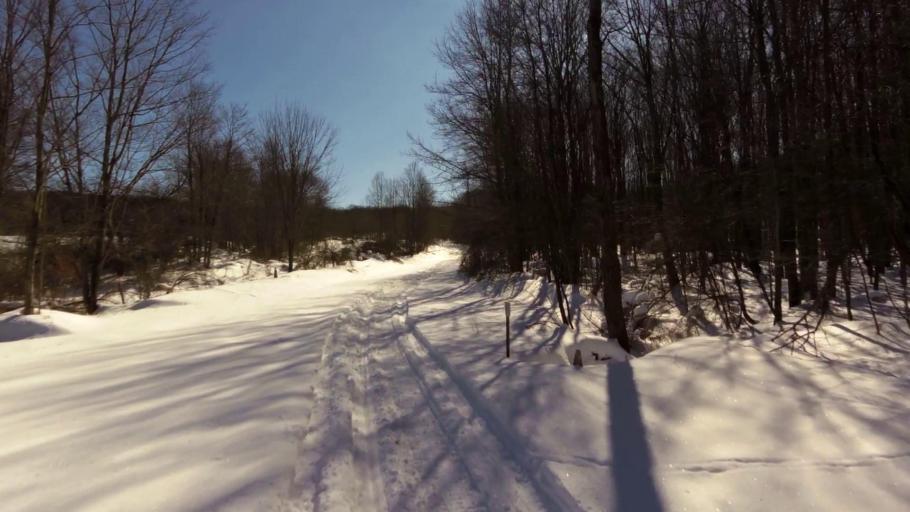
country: US
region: New York
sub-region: Allegany County
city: Cuba
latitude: 42.3315
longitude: -78.3011
